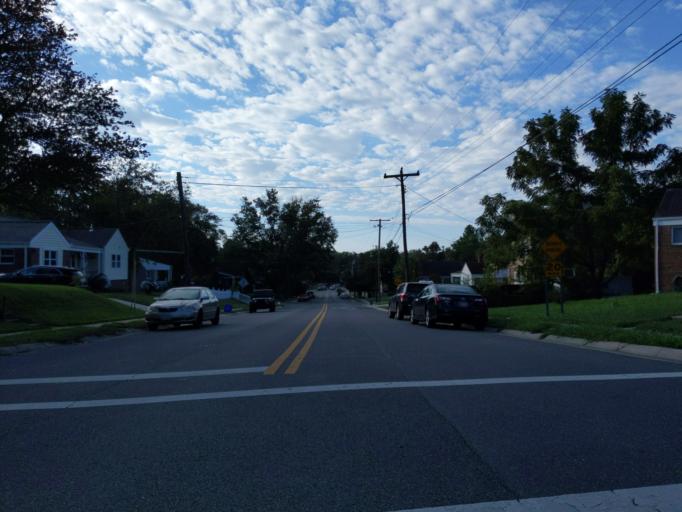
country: US
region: Maryland
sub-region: Montgomery County
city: Forest Glen
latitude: 39.0246
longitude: -77.0499
